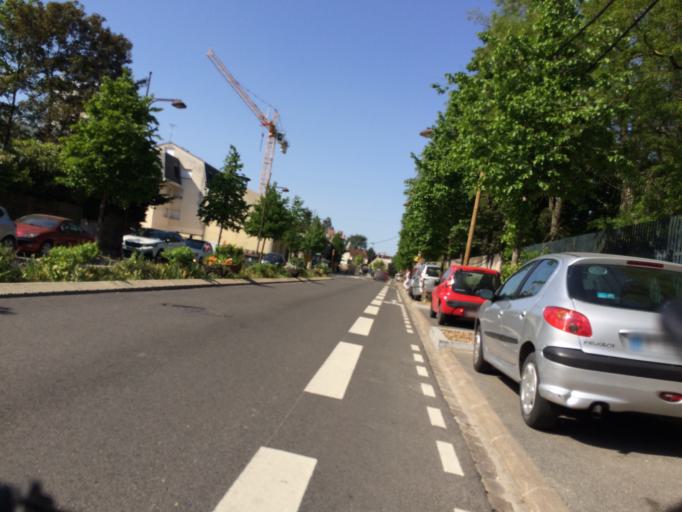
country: FR
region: Ile-de-France
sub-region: Departement des Hauts-de-Seine
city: Chatenay-Malabry
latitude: 48.7655
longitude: 2.2723
